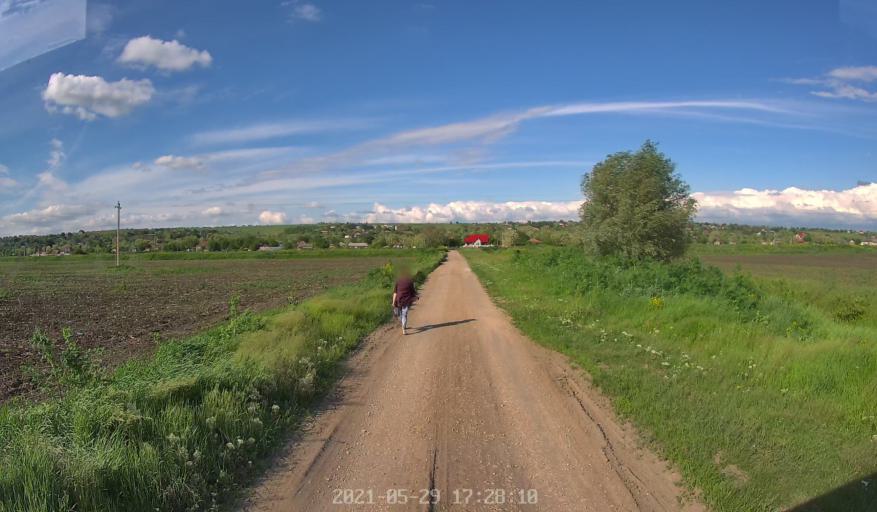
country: MD
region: Laloveni
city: Ialoveni
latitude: 46.8330
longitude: 28.8403
